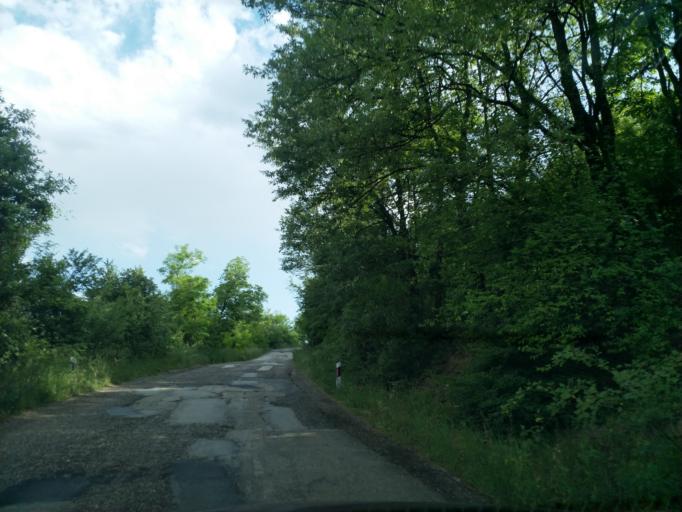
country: RS
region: Central Serbia
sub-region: Borski Okrug
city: Bor
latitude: 43.9944
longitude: 21.9783
